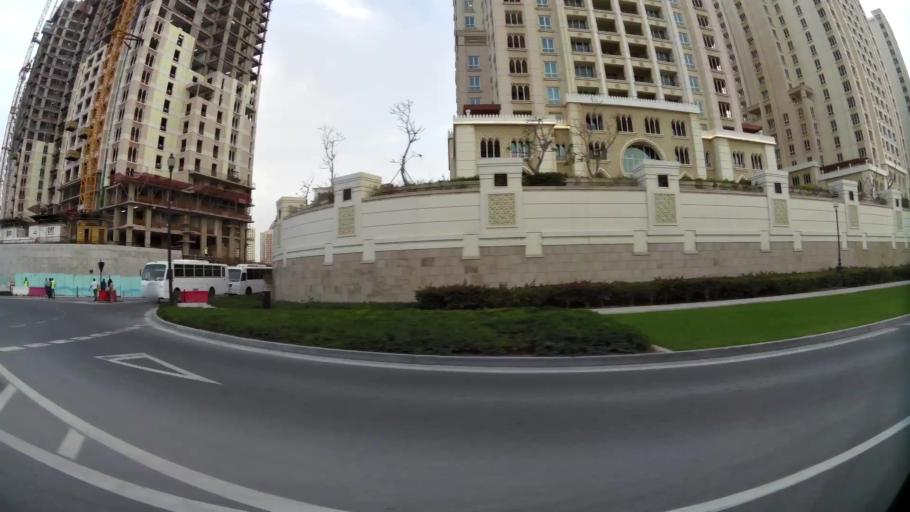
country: QA
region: Baladiyat ad Dawhah
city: Doha
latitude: 25.3708
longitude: 51.5569
